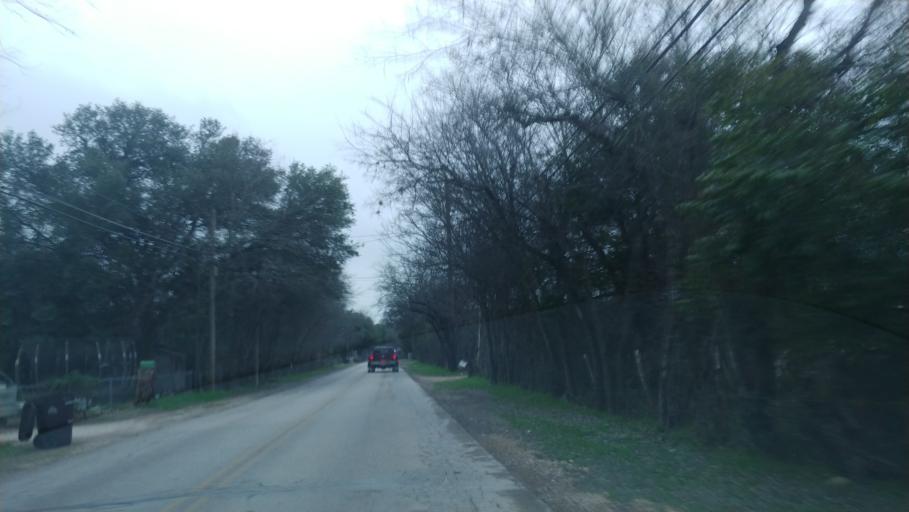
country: US
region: Texas
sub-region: Bexar County
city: Helotes
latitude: 29.6115
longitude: -98.6847
